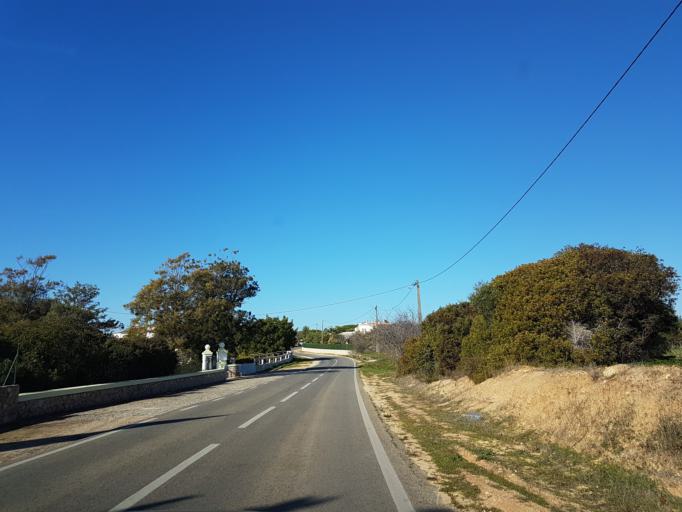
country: PT
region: Faro
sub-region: Lagoa
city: Carvoeiro
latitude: 37.0944
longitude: -8.4343
